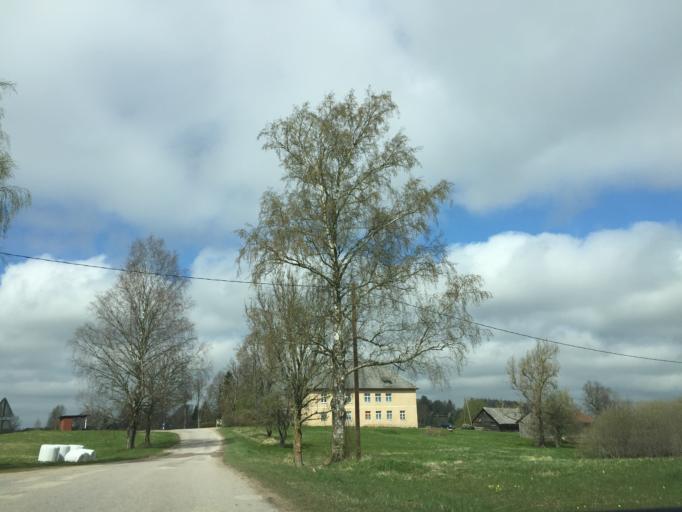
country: EE
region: Valgamaa
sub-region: Valga linn
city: Valga
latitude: 57.5443
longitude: 26.3012
